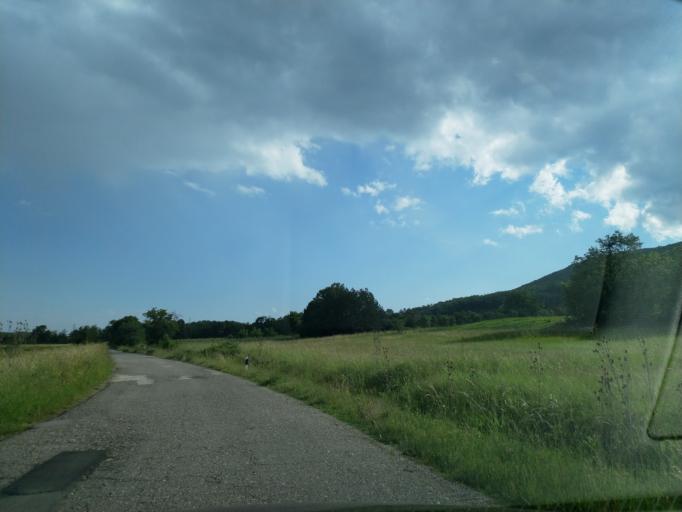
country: RS
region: Central Serbia
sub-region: Borski Okrug
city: Bor
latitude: 43.9847
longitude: 21.9737
